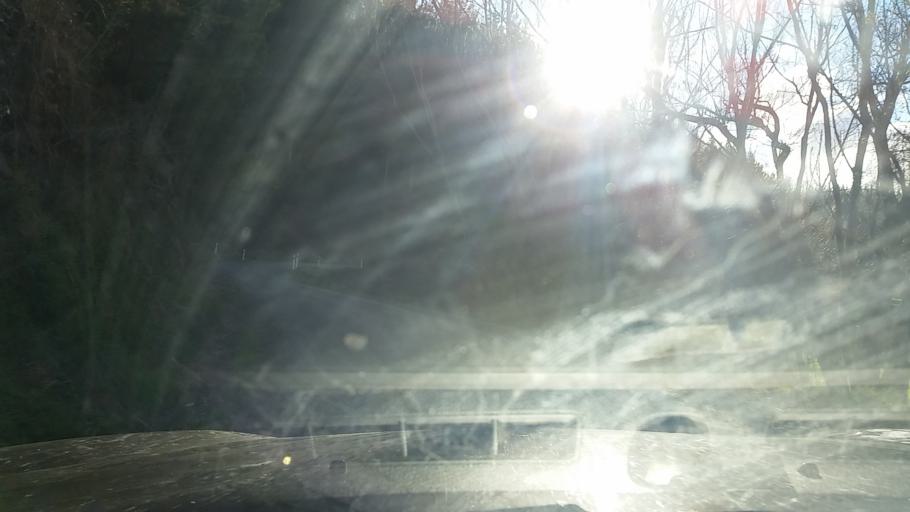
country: NZ
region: Nelson
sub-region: Nelson City
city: Nelson
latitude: -41.5610
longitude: 173.4316
